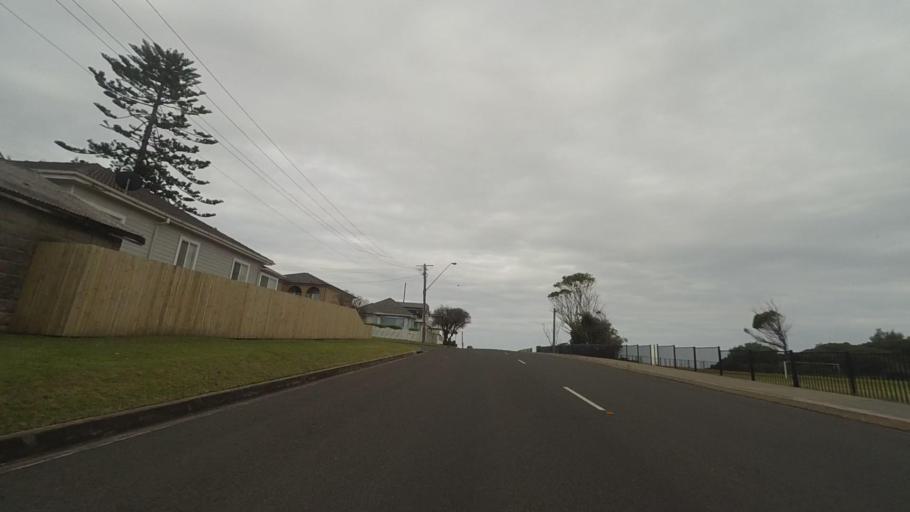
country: AU
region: New South Wales
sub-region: Wollongong
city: Port Kembla
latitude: -34.4883
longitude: 150.9134
